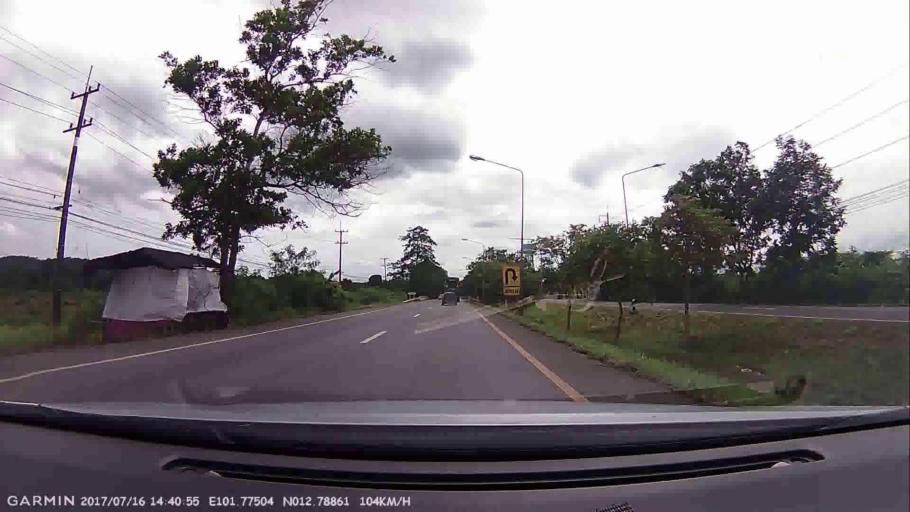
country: TH
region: Chanthaburi
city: Na Yai Am
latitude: 12.7886
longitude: 101.7748
